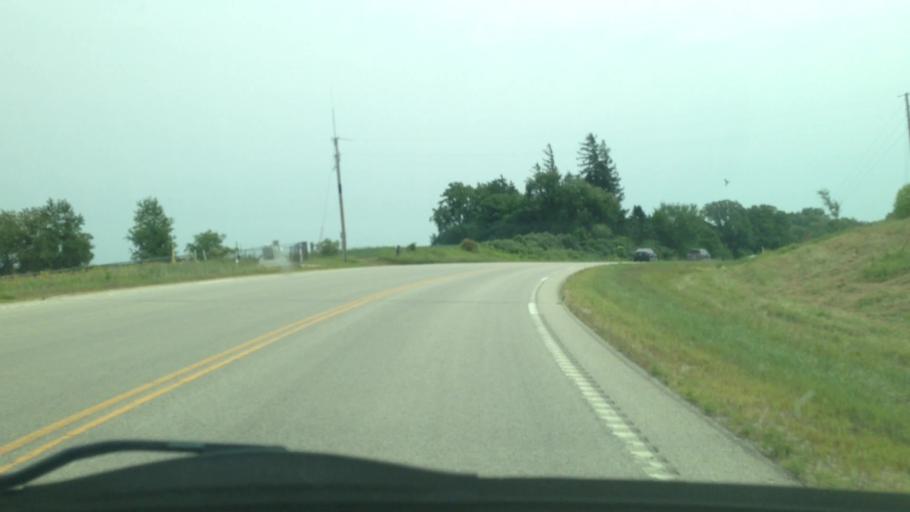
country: US
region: Minnesota
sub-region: Fillmore County
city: Preston
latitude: 43.7283
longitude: -91.9856
